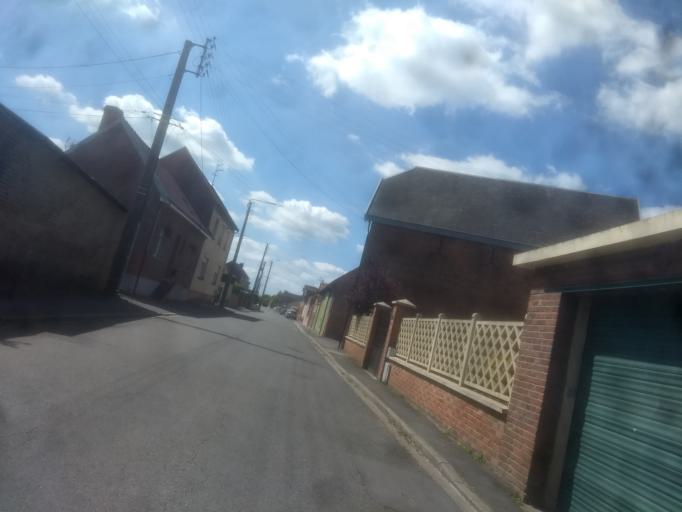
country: FR
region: Nord-Pas-de-Calais
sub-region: Departement du Pas-de-Calais
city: Agny
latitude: 50.2587
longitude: 2.7591
